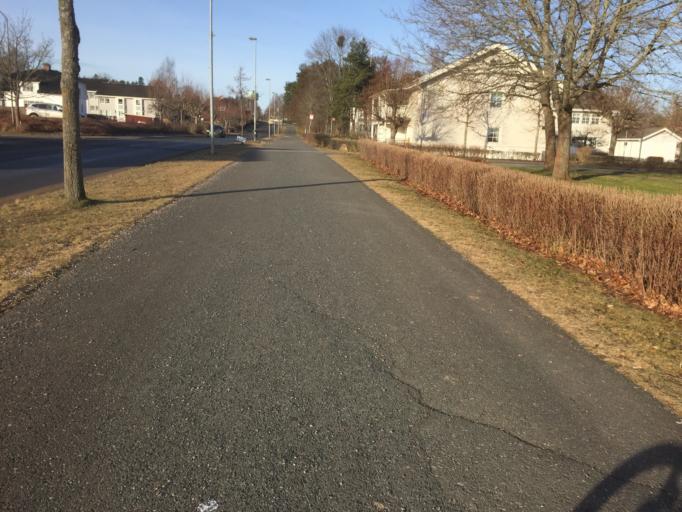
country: SE
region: Joenkoeping
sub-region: Aneby Kommun
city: Aneby
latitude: 57.8384
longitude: 14.8105
